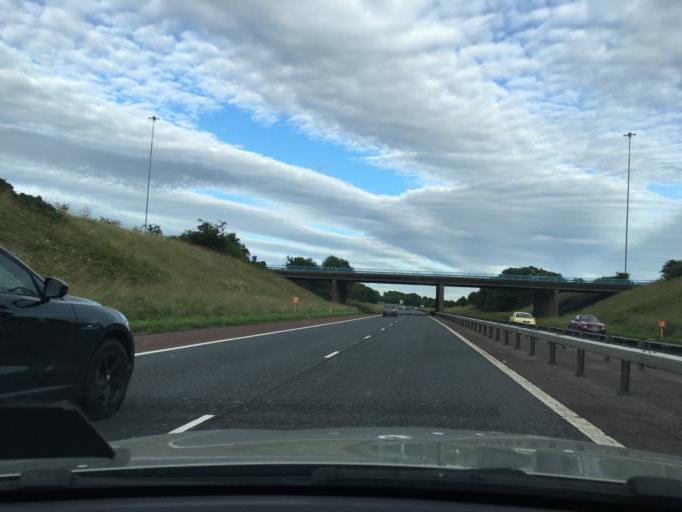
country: GB
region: Northern Ireland
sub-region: Antrim Borough
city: Antrim
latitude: 54.7250
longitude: -6.1593
